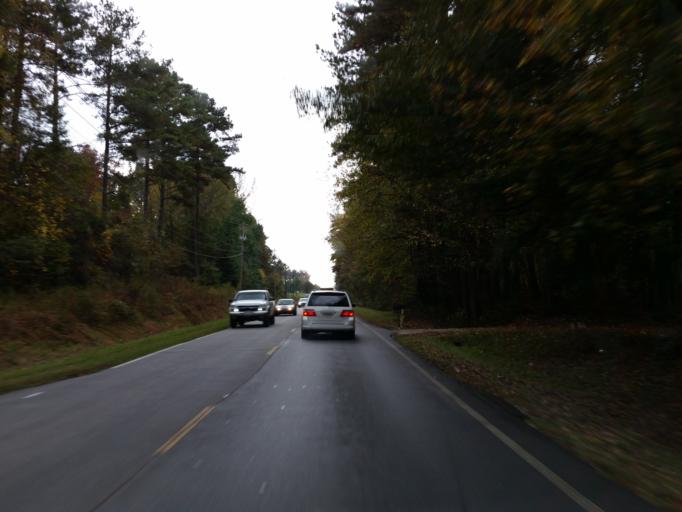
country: US
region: Georgia
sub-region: Henry County
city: Stockbridge
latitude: 33.5103
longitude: -84.2451
